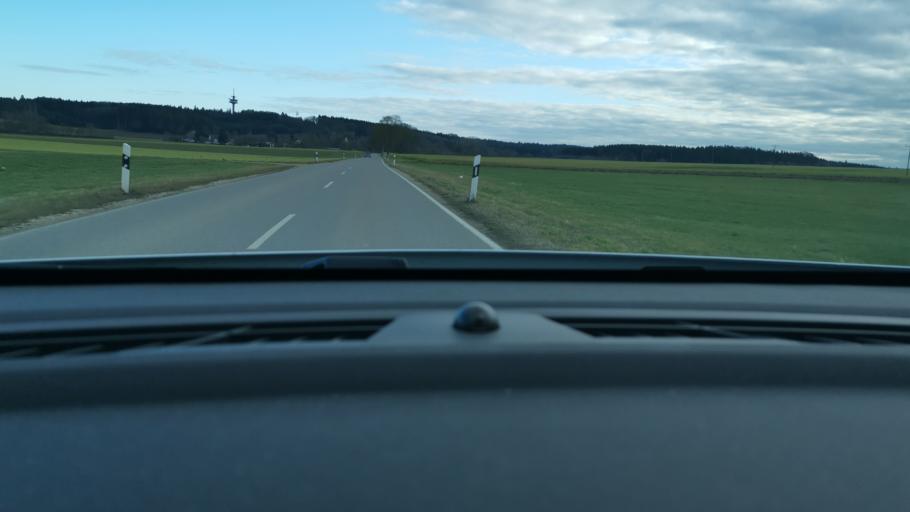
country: DE
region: Bavaria
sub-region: Swabia
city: Affing
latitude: 48.4967
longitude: 11.0020
